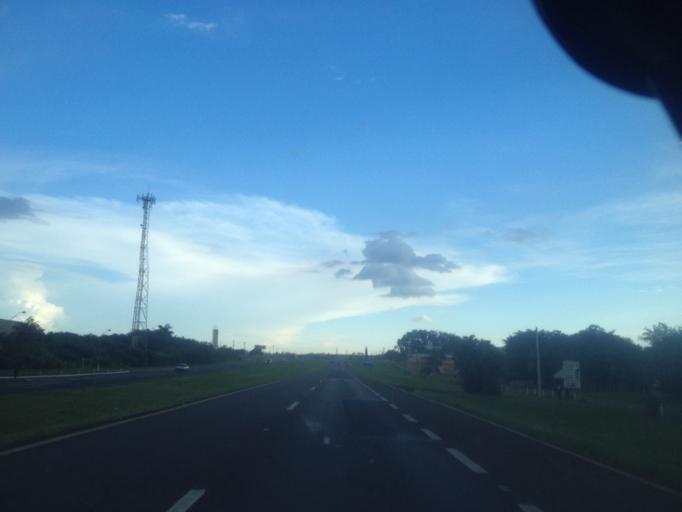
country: BR
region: Sao Paulo
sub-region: Leme
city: Leme
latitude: -22.2180
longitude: -47.3927
